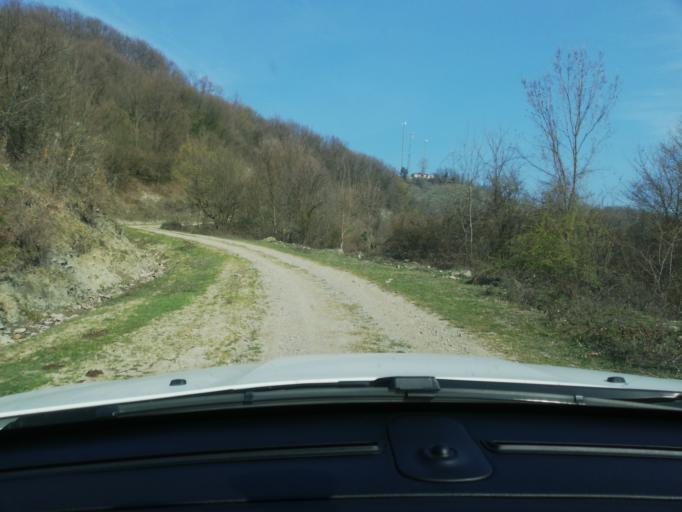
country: TR
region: Karabuk
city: Yenice
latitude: 41.2692
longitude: 32.3571
